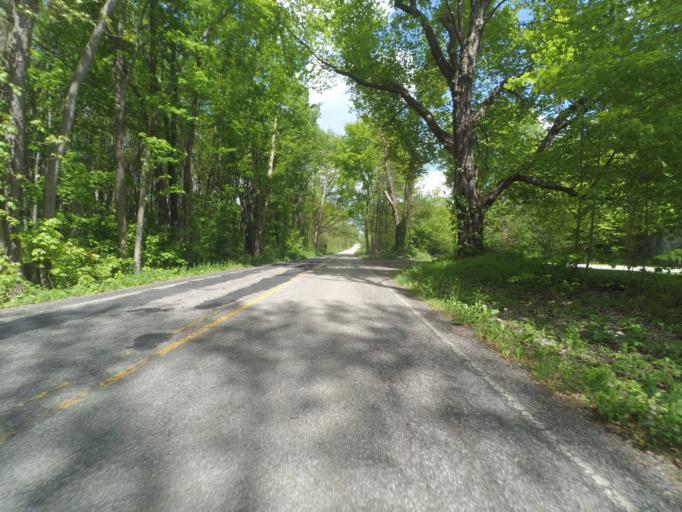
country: US
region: Ohio
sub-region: Trumbull County
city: Lordstown
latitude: 41.1274
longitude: -80.8822
